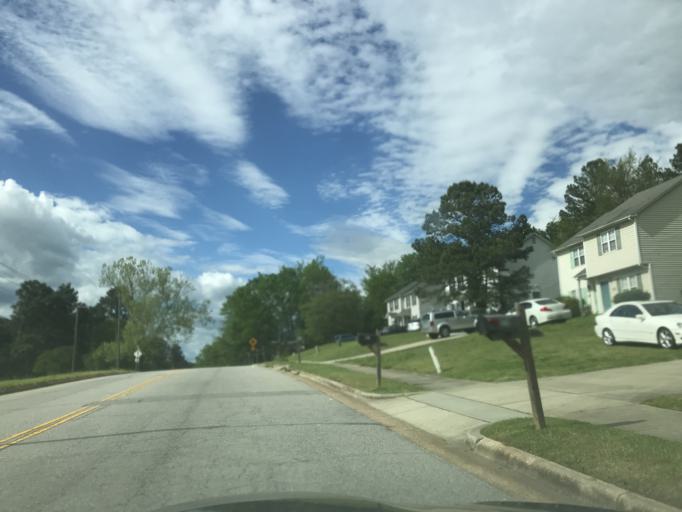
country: US
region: North Carolina
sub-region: Wake County
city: Raleigh
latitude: 35.7795
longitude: -78.5918
